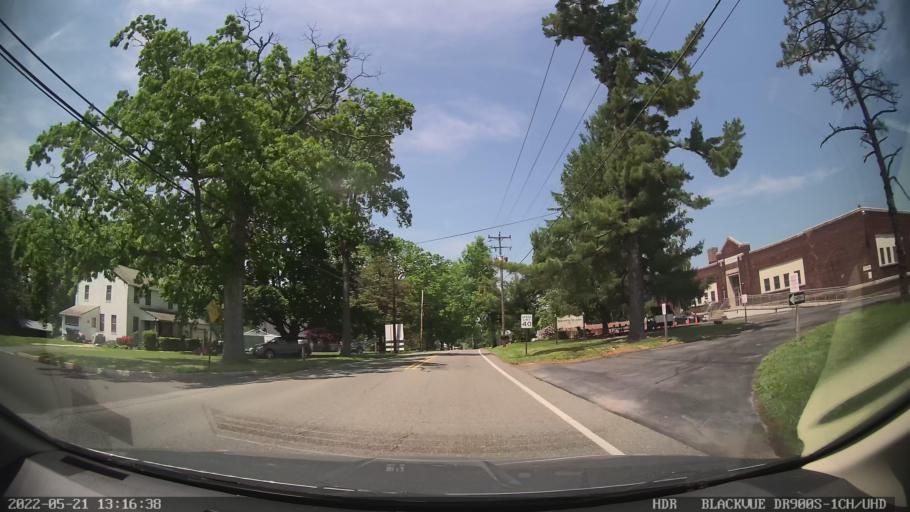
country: US
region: Pennsylvania
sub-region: Montgomery County
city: Gilbertsville
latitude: 40.3523
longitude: -75.5863
